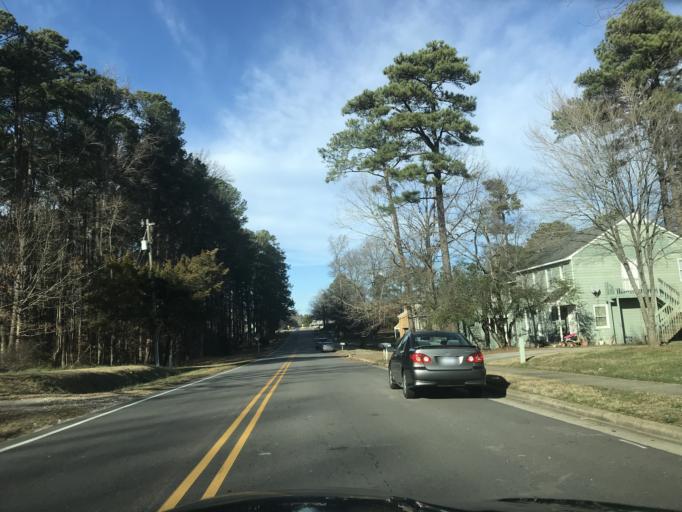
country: US
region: North Carolina
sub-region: Wake County
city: Cary
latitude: 35.7859
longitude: -78.7429
